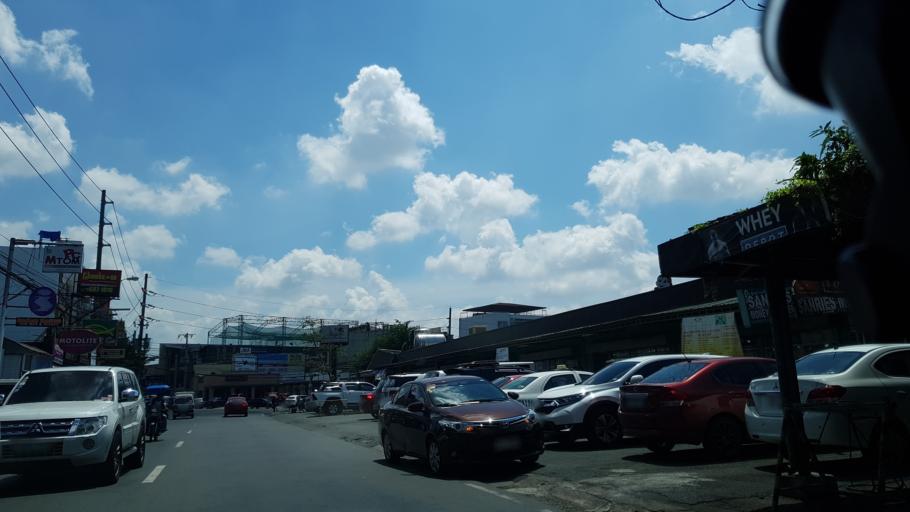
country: PH
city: Sambayanihan People's Village
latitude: 14.4460
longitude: 121.0288
